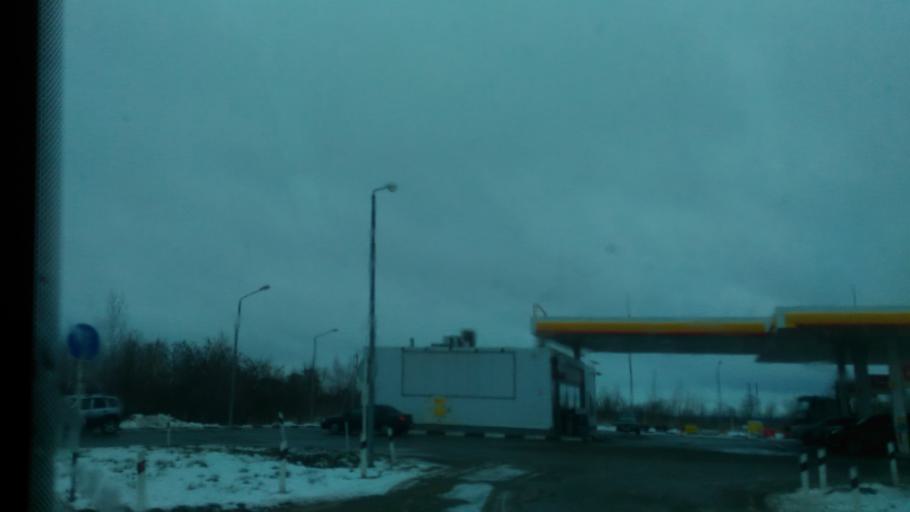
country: RU
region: Tula
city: Bolokhovo
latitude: 54.0612
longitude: 37.8030
